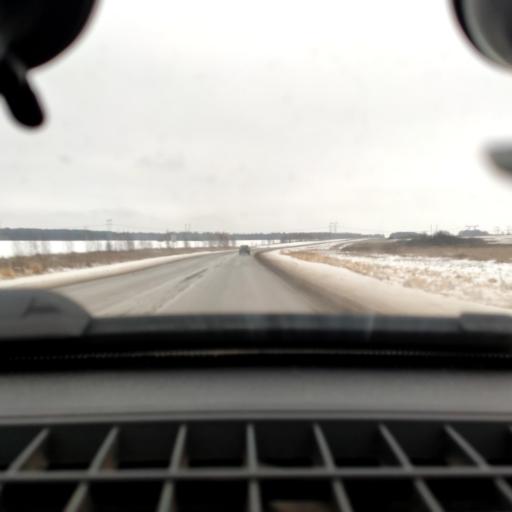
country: RU
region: Bashkortostan
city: Iglino
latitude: 54.7889
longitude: 56.4177
